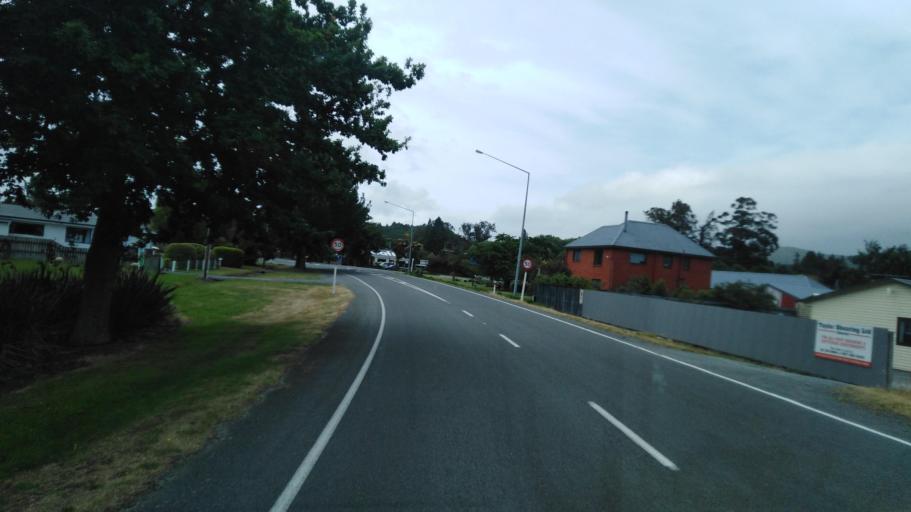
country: NZ
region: Canterbury
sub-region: Kaikoura District
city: Kaikoura
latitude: -42.8160
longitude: 173.2727
